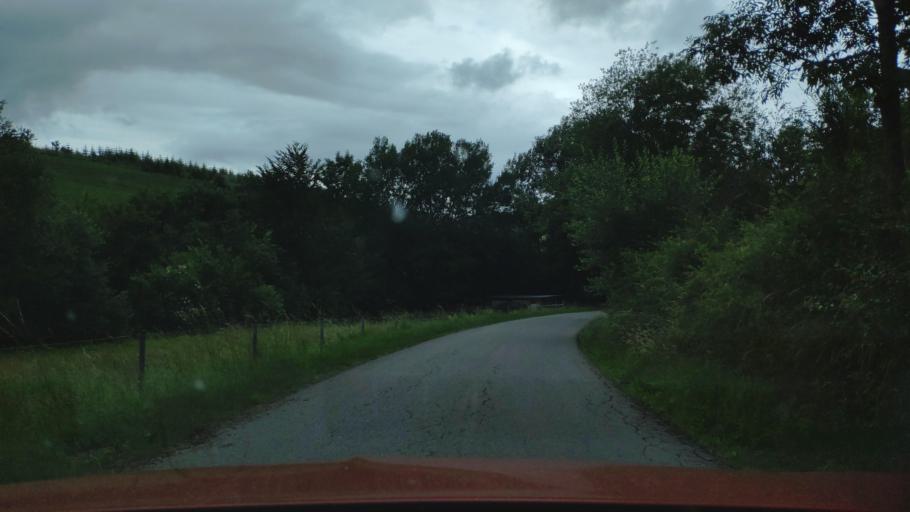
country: DE
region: North Rhine-Westphalia
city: Eslohe
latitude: 51.2096
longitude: 8.0880
